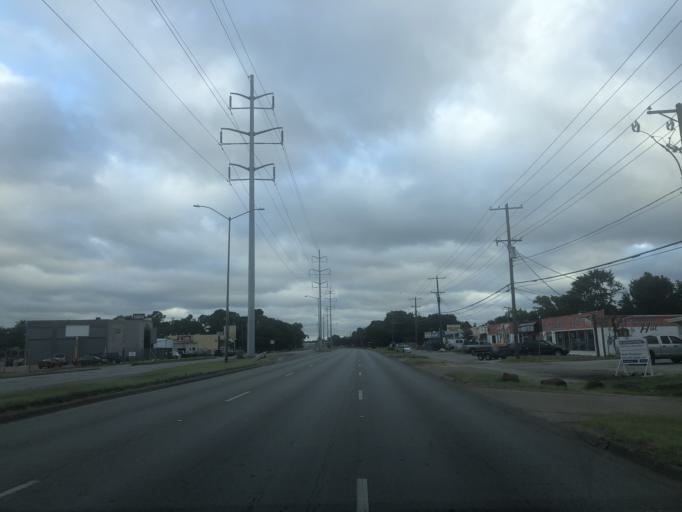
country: US
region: Texas
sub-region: Dallas County
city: University Park
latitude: 32.8282
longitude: -96.8567
